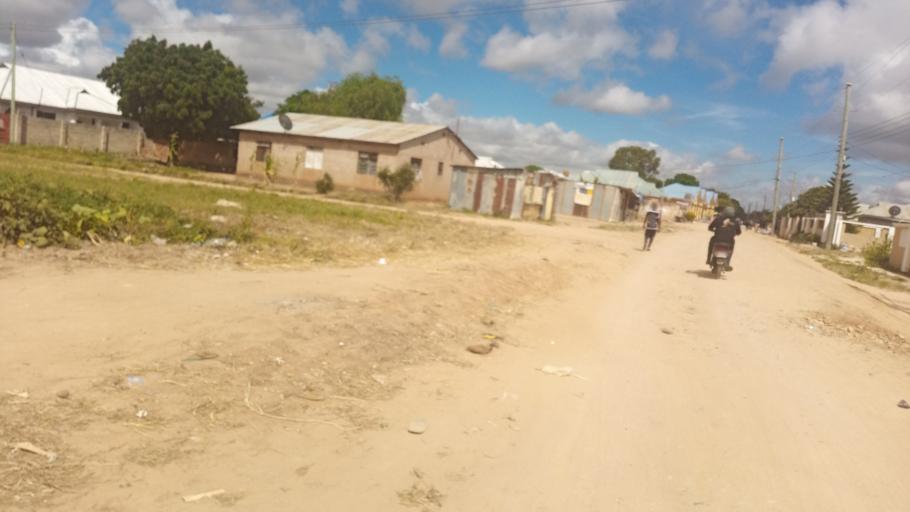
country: TZ
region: Dodoma
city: Kisasa
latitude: -6.1754
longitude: 35.7710
